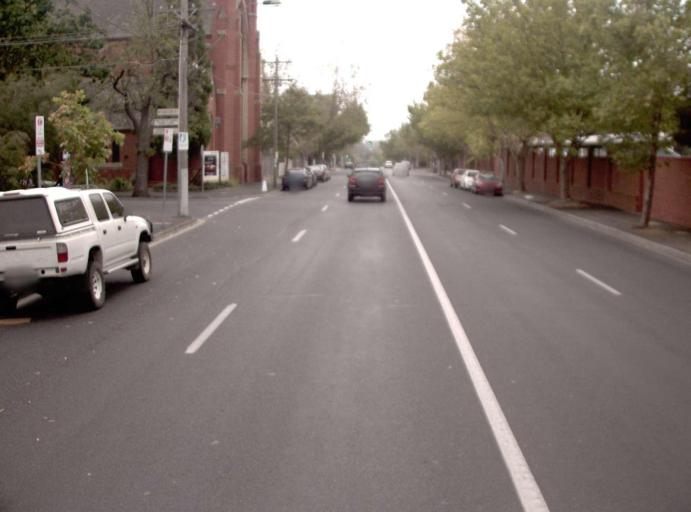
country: AU
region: Victoria
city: Toorak
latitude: -37.8533
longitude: 145.0117
